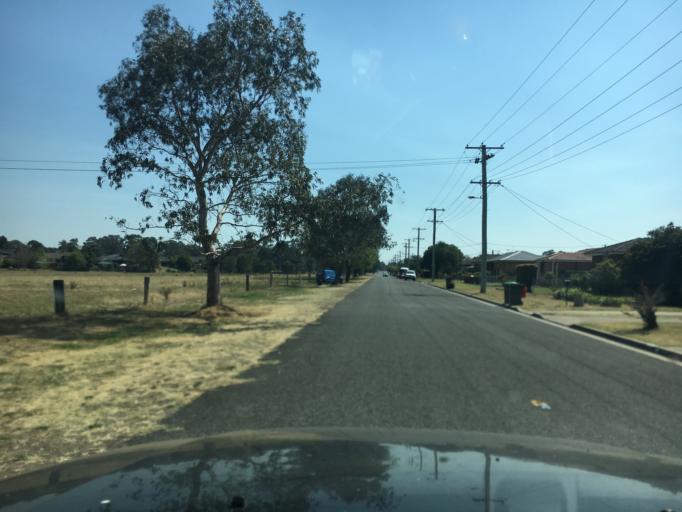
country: AU
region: New South Wales
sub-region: Singleton
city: Singleton
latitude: -32.5724
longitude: 151.1886
